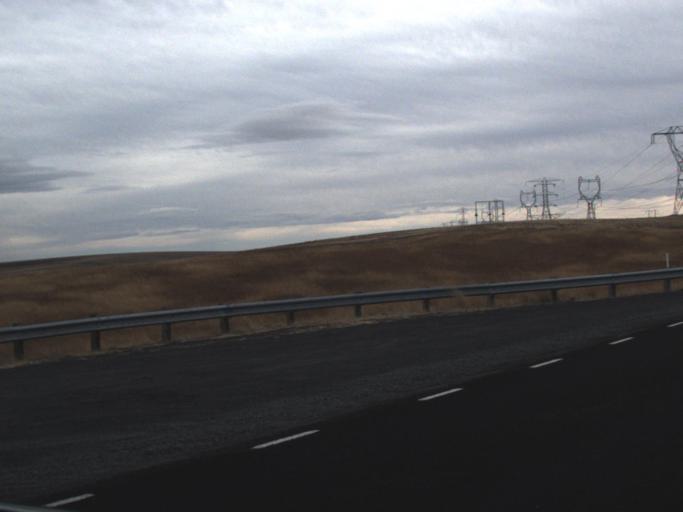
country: US
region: Washington
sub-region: Okanogan County
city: Coulee Dam
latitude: 47.8810
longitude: -118.8506
